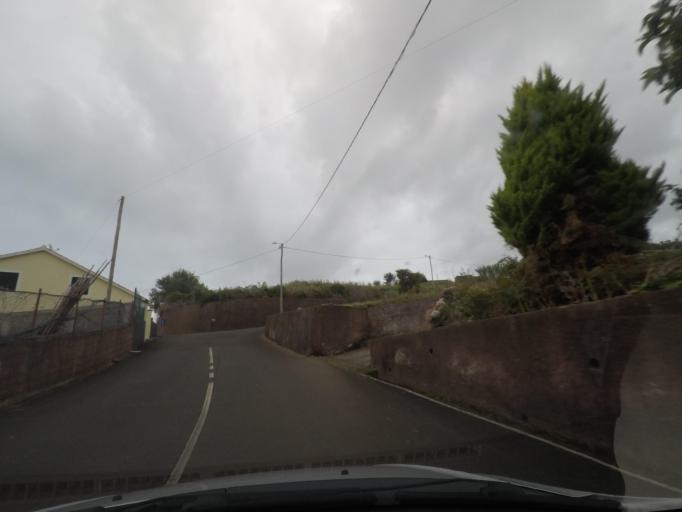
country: PT
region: Madeira
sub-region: Santana
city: Santana
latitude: 32.8181
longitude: -16.8845
